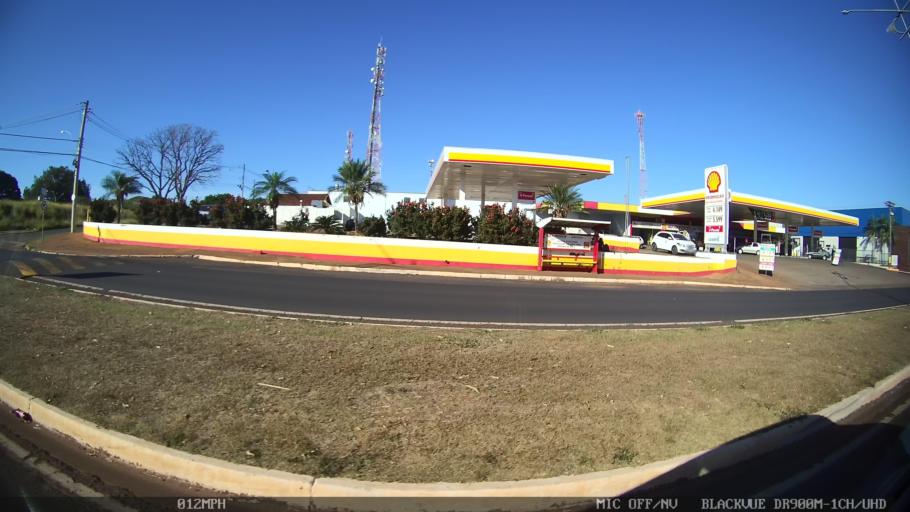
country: BR
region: Sao Paulo
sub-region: Olimpia
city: Olimpia
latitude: -20.7287
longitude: -48.9053
